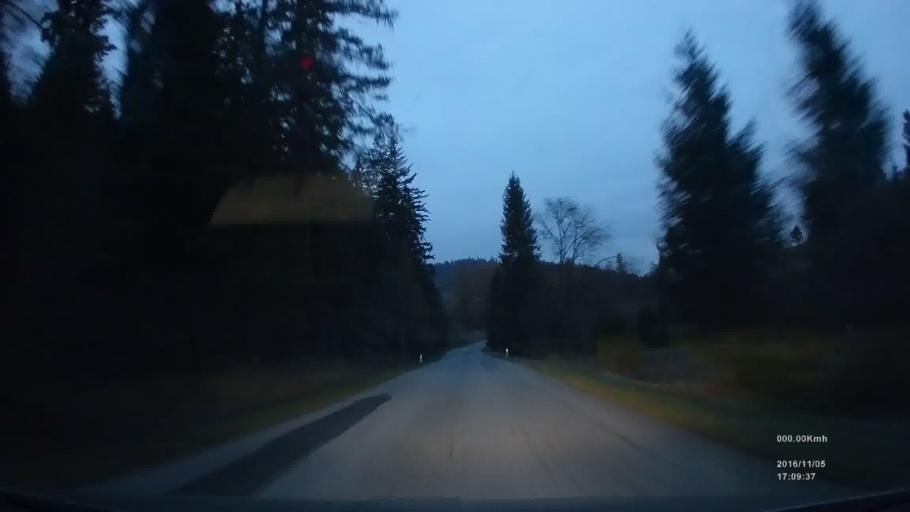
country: SK
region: Presovsky
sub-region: Okres Presov
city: Levoca
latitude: 49.0561
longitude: 20.5137
